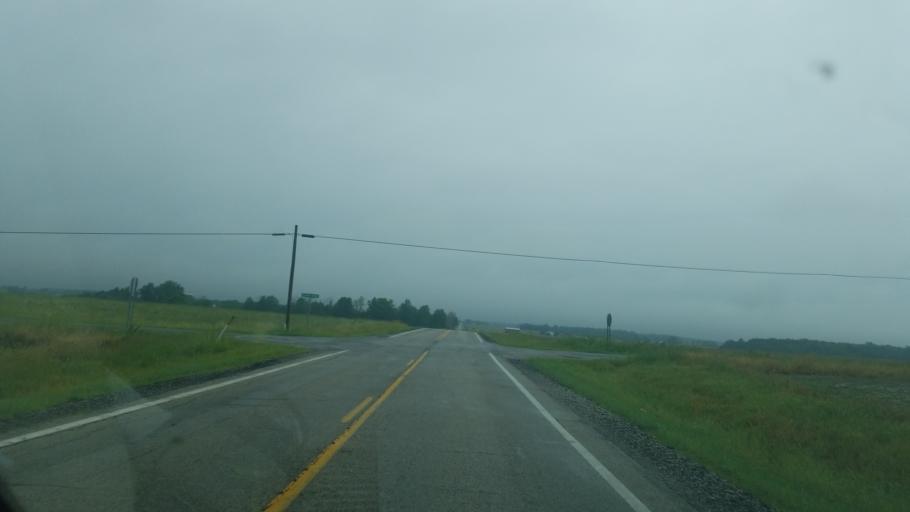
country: US
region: Ohio
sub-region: Crawford County
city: Bucyrus
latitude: 40.8734
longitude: -82.8548
